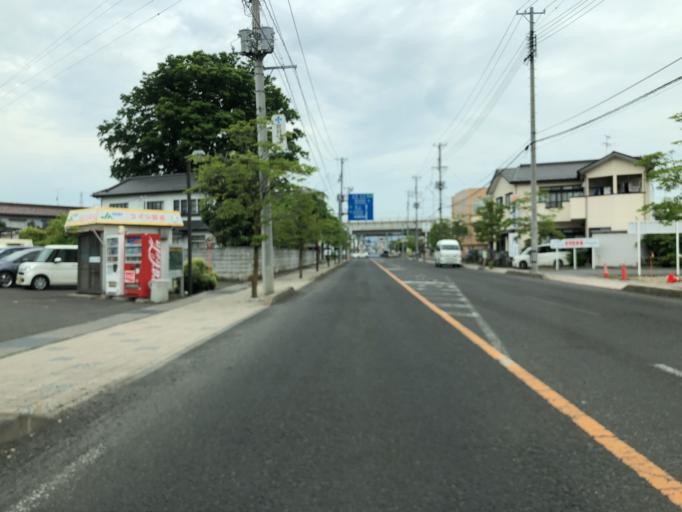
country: JP
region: Fukushima
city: Fukushima-shi
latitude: 37.7758
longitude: 140.4475
